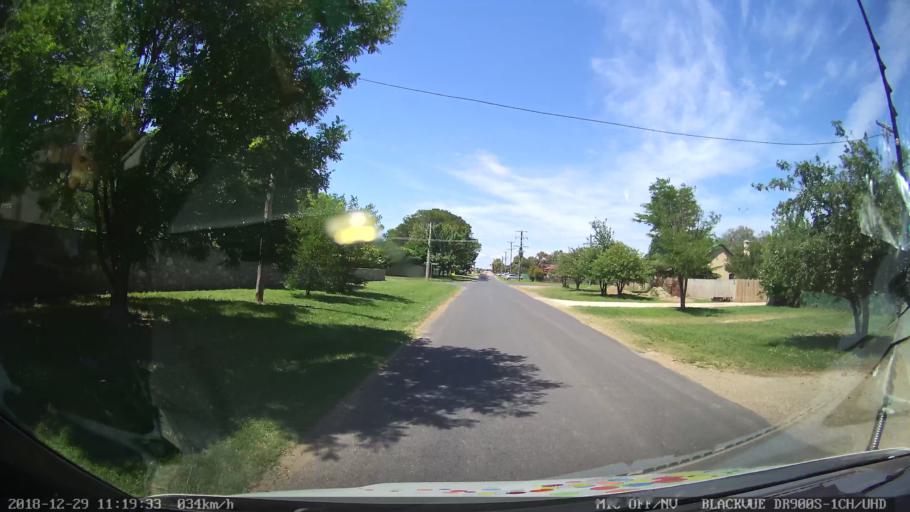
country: AU
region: New South Wales
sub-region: Palerang
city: Bungendore
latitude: -35.2581
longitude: 149.4431
